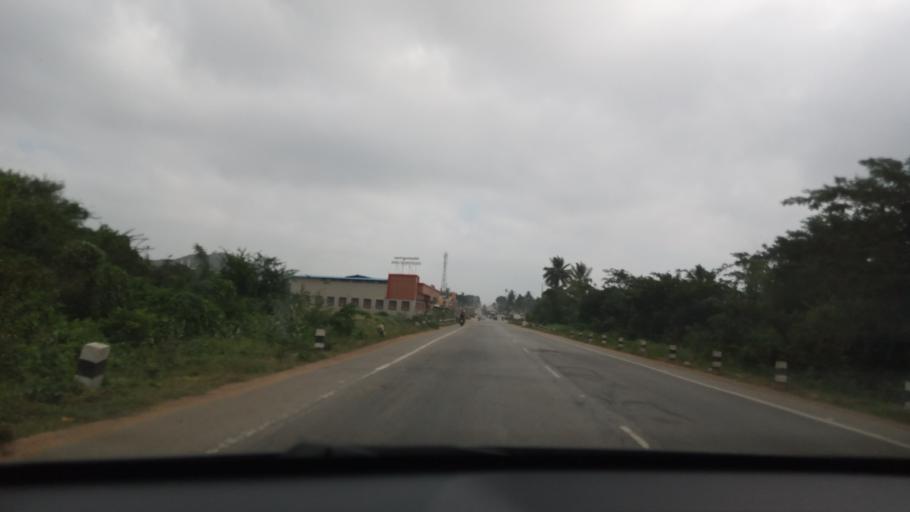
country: IN
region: Karnataka
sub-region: Chikkaballapur
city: Chintamani
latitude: 13.3536
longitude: 78.0299
